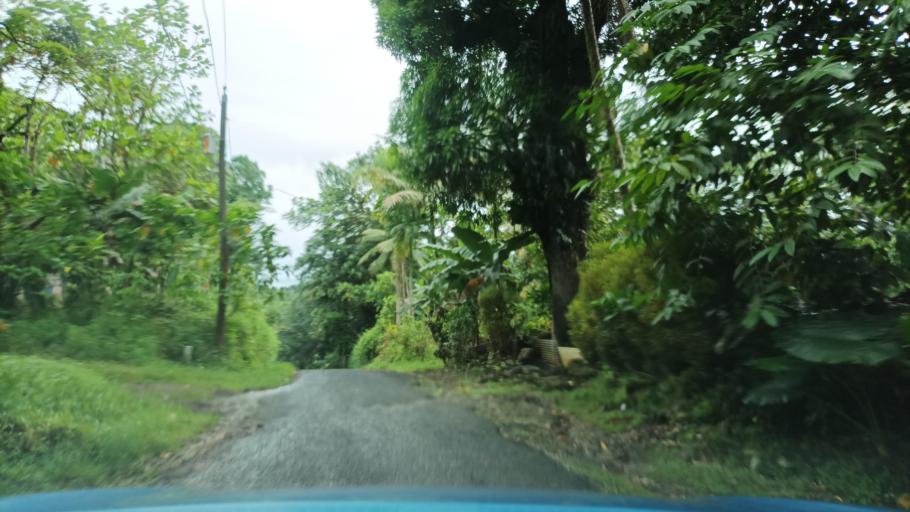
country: FM
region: Pohnpei
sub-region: Sokehs Municipality
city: Palikir - National Government Center
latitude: 6.8297
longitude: 158.1705
